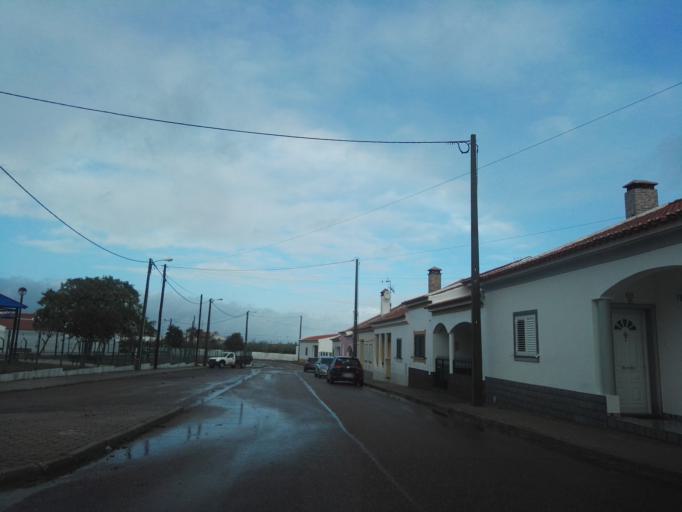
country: PT
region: Portalegre
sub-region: Elvas
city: Elvas
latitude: 38.9512
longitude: -7.2123
